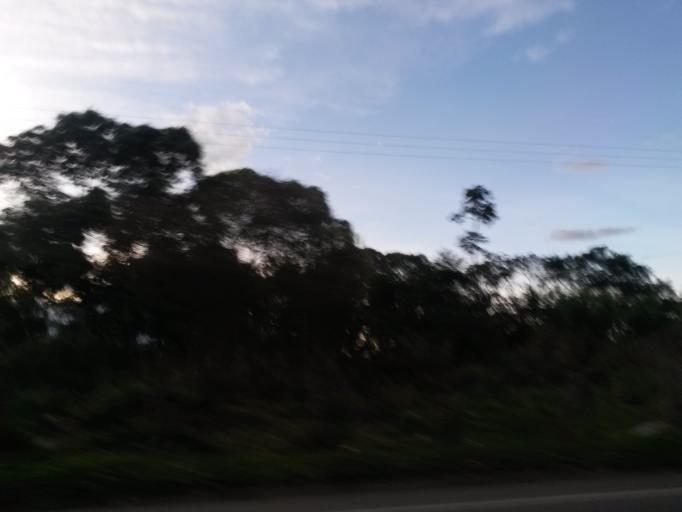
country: CO
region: Cauca
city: Popayan
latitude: 2.4776
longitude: -76.6131
